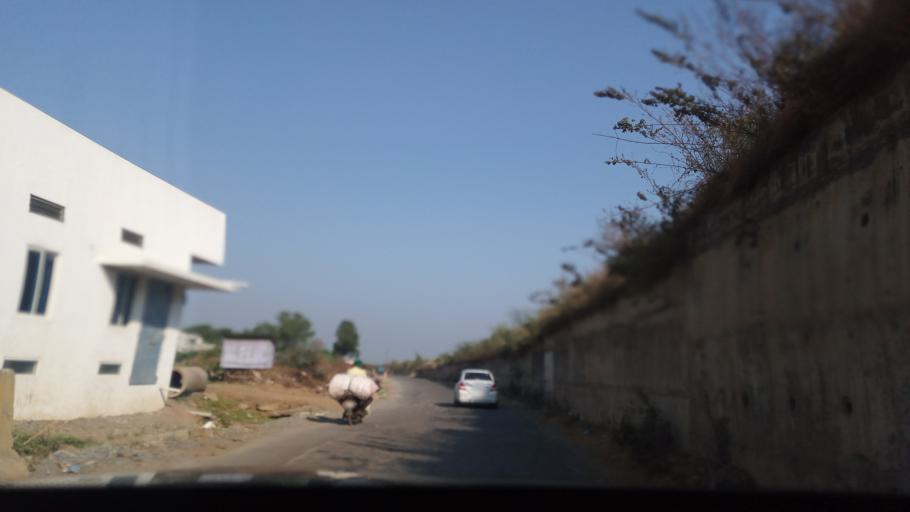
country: IN
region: Karnataka
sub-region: Haveri
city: Byadgi
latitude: 14.7193
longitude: 75.4811
